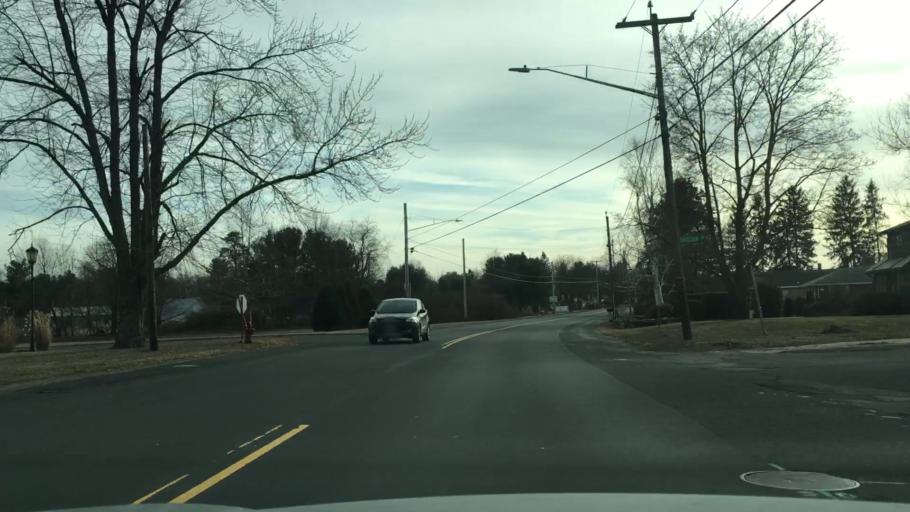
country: US
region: Massachusetts
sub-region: Hampden County
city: Westfield
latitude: 42.0916
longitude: -72.7629
